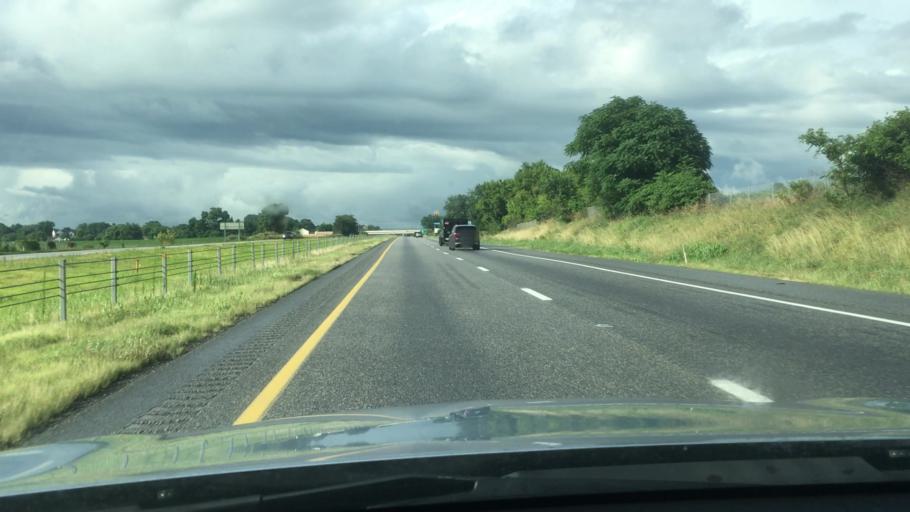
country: US
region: Pennsylvania
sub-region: Franklin County
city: Scotland
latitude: 39.9557
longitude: -77.5815
